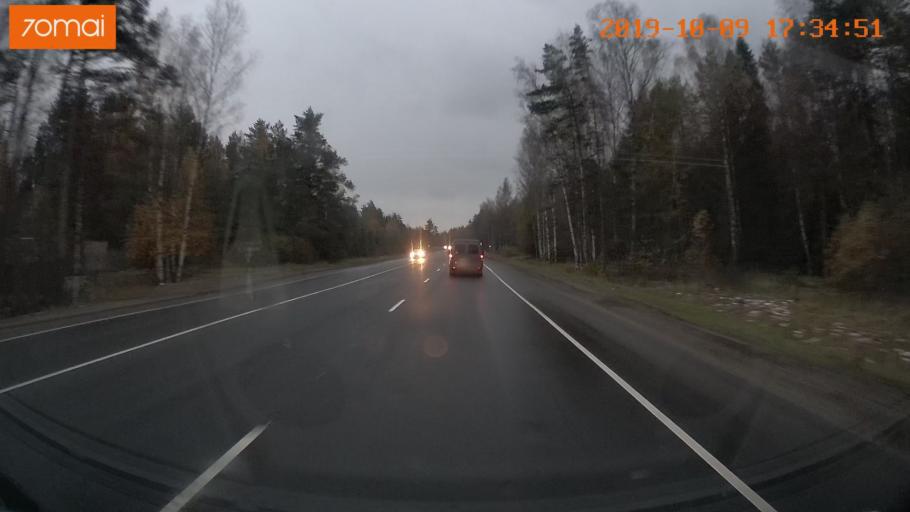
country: RU
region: Ivanovo
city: Bogorodskoye
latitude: 57.1024
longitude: 41.0079
